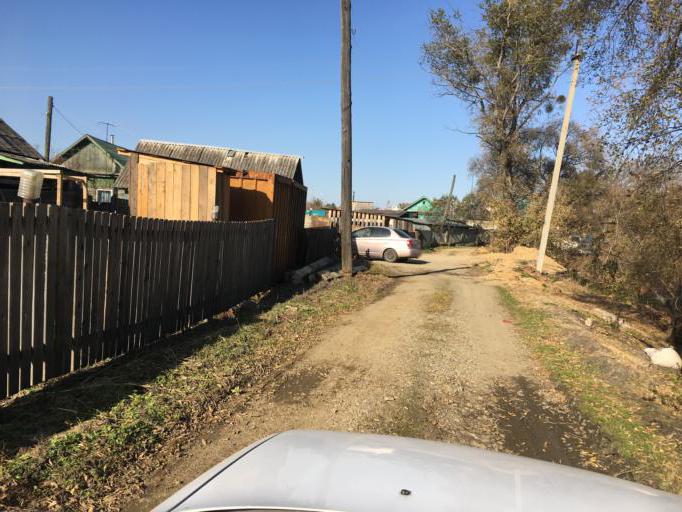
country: RU
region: Primorskiy
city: Dal'nerechensk
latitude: 45.9271
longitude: 133.7267
